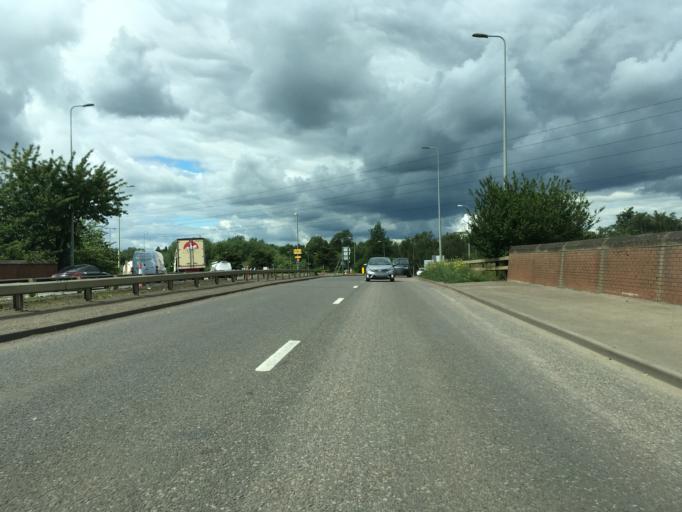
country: GB
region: England
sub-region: Oxfordshire
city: Banbury
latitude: 52.0714
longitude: -1.3291
